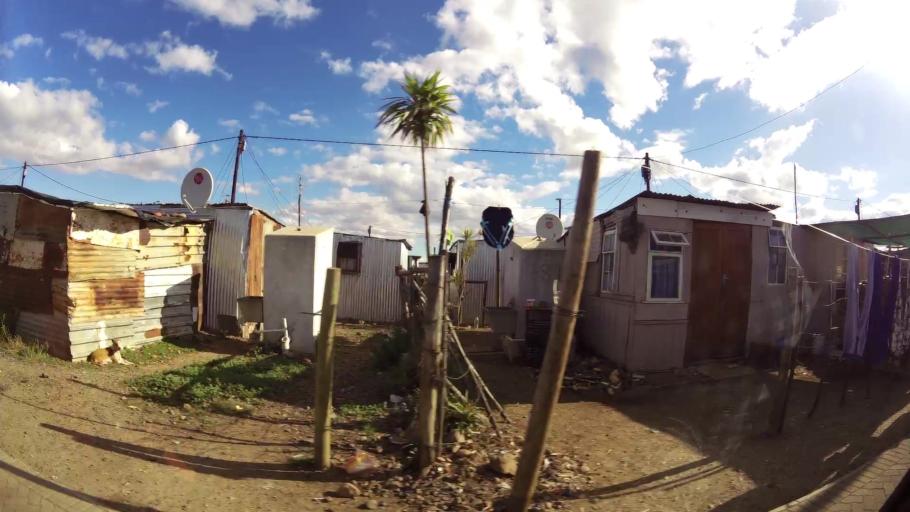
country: ZA
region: Western Cape
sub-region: Overberg District Municipality
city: Swellendam
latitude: -34.0491
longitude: 20.4395
